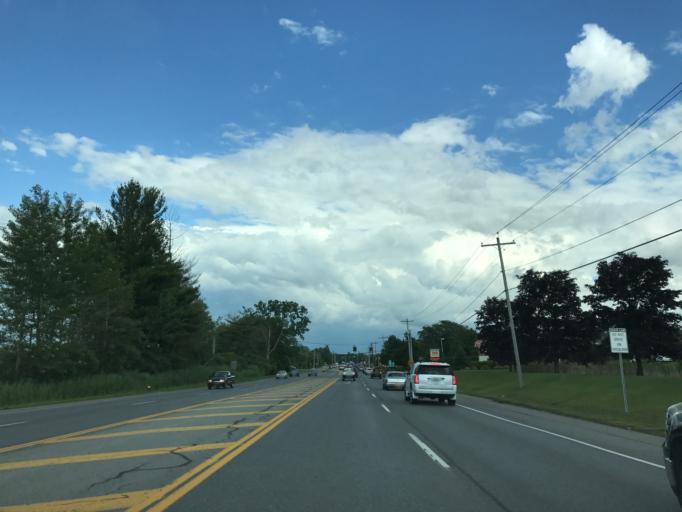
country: US
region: New York
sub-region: Warren County
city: Glens Falls
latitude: 43.3320
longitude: -73.6565
